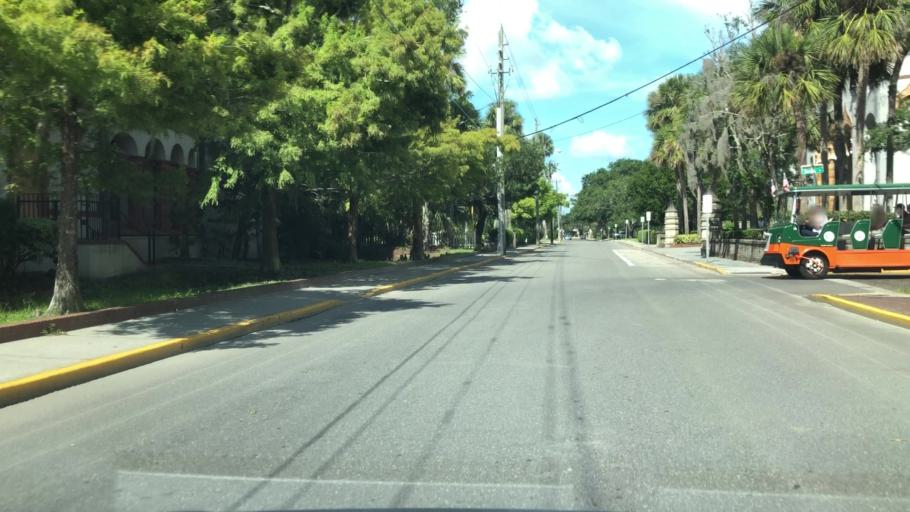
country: US
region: Florida
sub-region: Saint Johns County
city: Saint Augustine
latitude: 29.8935
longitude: -81.3162
